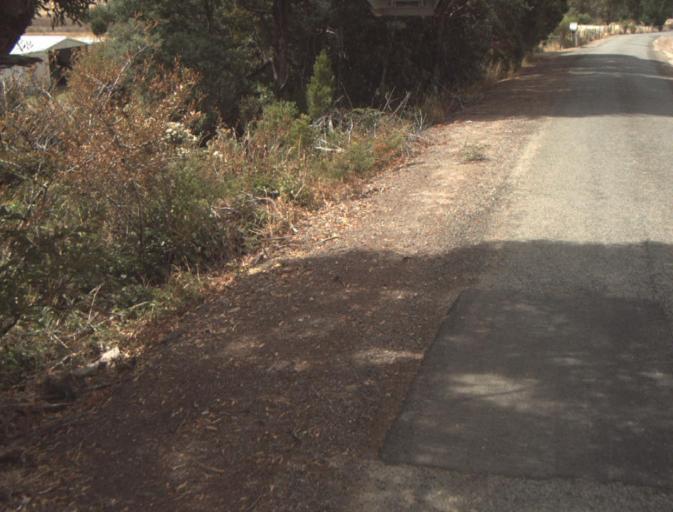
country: AU
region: Tasmania
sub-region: Northern Midlands
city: Evandale
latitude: -41.4607
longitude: 147.4483
